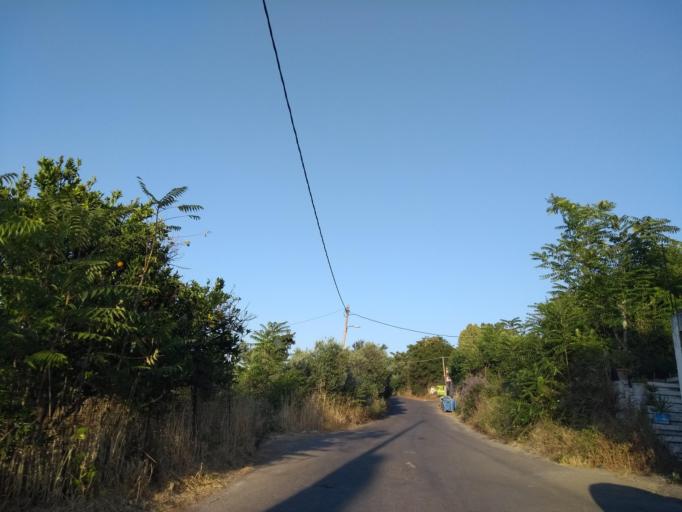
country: GR
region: Crete
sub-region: Nomos Chanias
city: Kalivai
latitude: 35.4077
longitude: 24.1999
